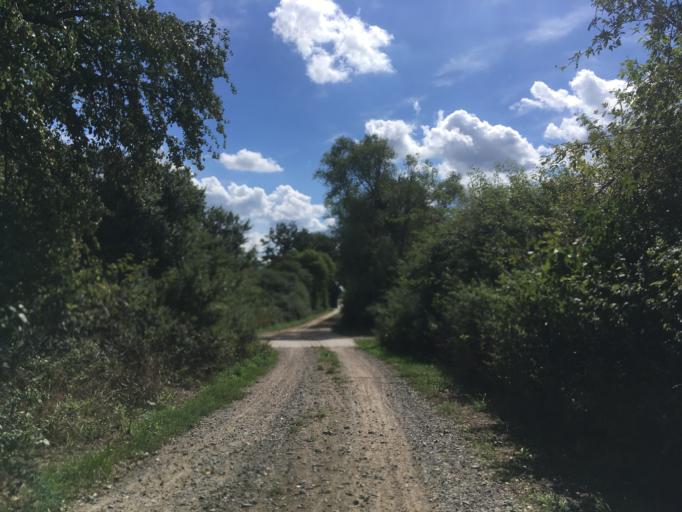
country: DE
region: Brandenburg
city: Gerswalde
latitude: 53.1041
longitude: 13.8664
